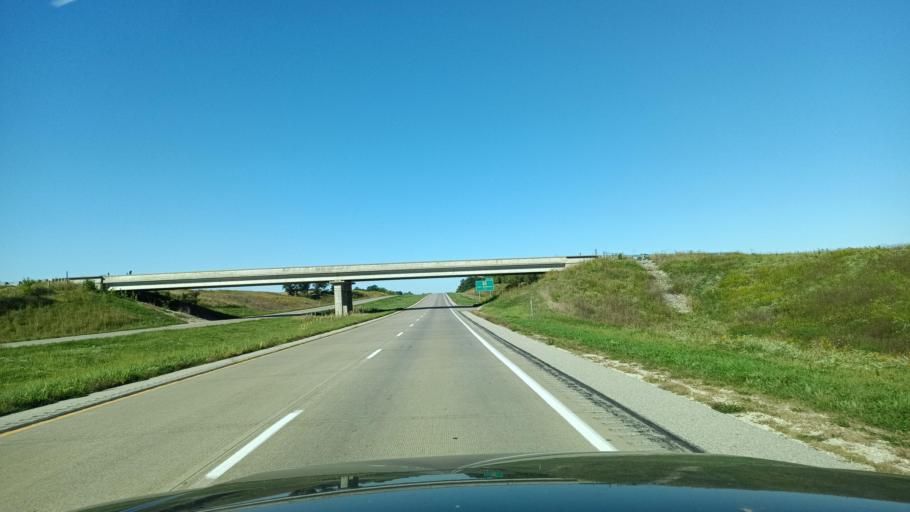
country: US
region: Iowa
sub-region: Lee County
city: Fort Madison
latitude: 40.6707
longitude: -91.2999
